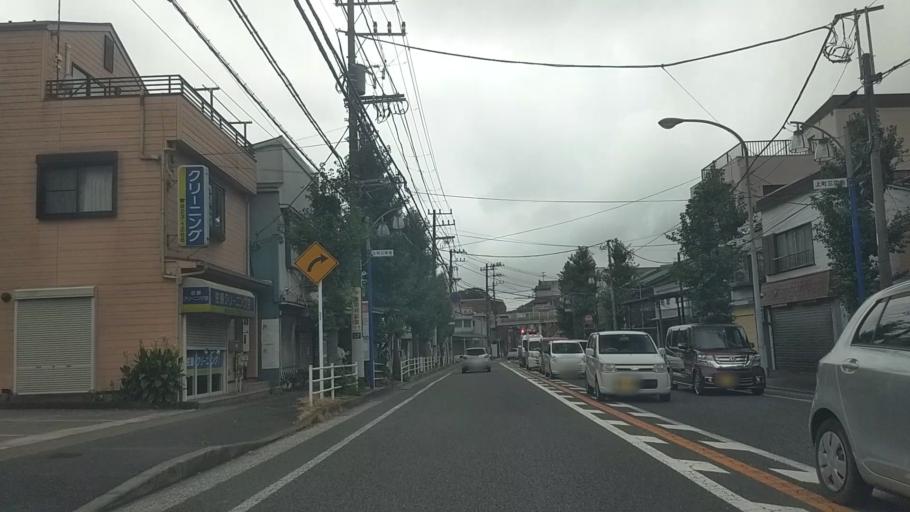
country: JP
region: Kanagawa
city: Yokosuka
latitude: 35.2703
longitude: 139.6717
